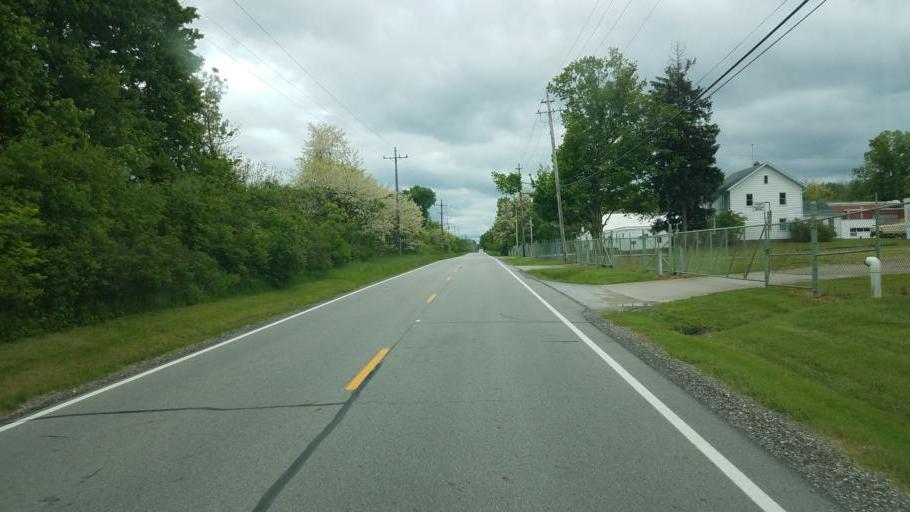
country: US
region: Ohio
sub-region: Geauga County
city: Burton
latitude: 41.4064
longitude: -81.1716
